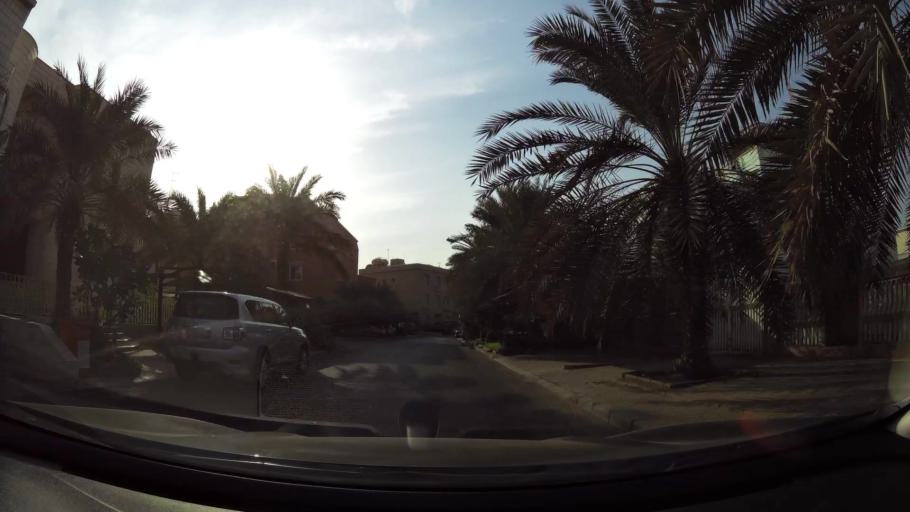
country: KW
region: Muhafazat Hawalli
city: Hawalli
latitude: 29.3076
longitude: 48.0019
